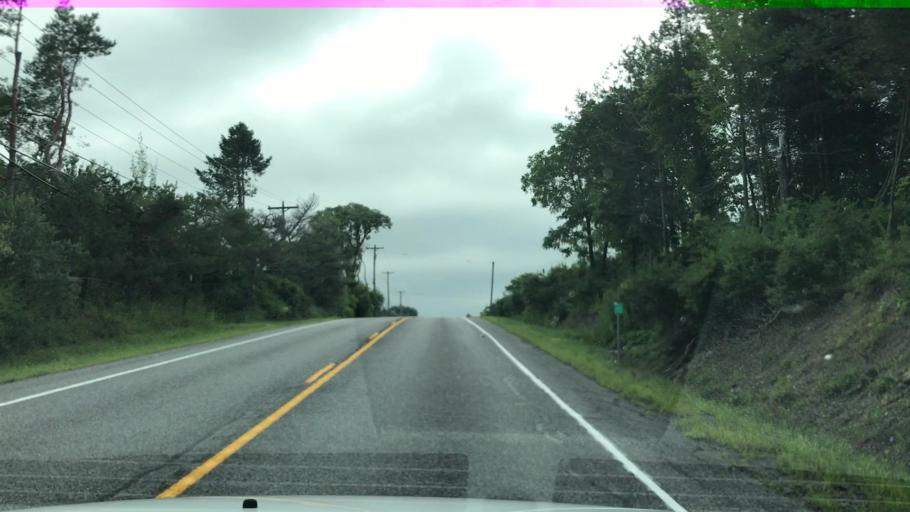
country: US
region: New York
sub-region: Wyoming County
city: Attica
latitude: 42.8360
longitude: -78.3690
